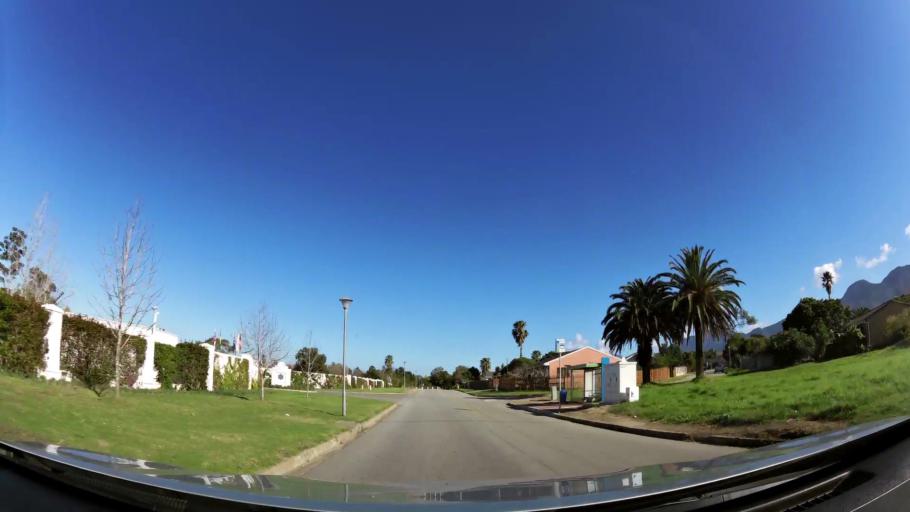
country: ZA
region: Western Cape
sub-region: Eden District Municipality
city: George
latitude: -33.9498
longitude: 22.4133
